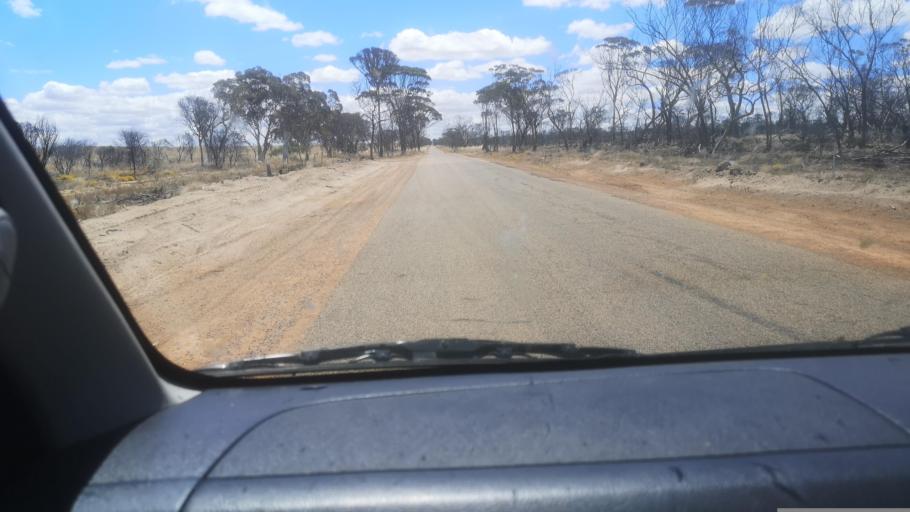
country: AU
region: Western Australia
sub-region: Cunderdin
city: Cunderdin
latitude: -32.1897
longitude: 117.6619
